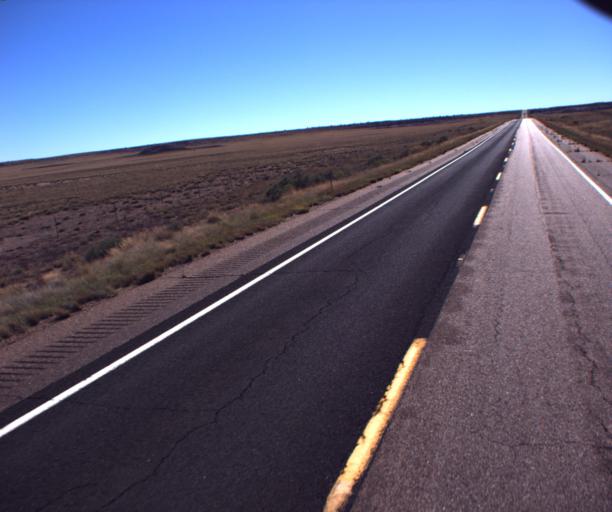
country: US
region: Arizona
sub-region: Navajo County
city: Snowflake
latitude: 34.7309
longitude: -109.7826
